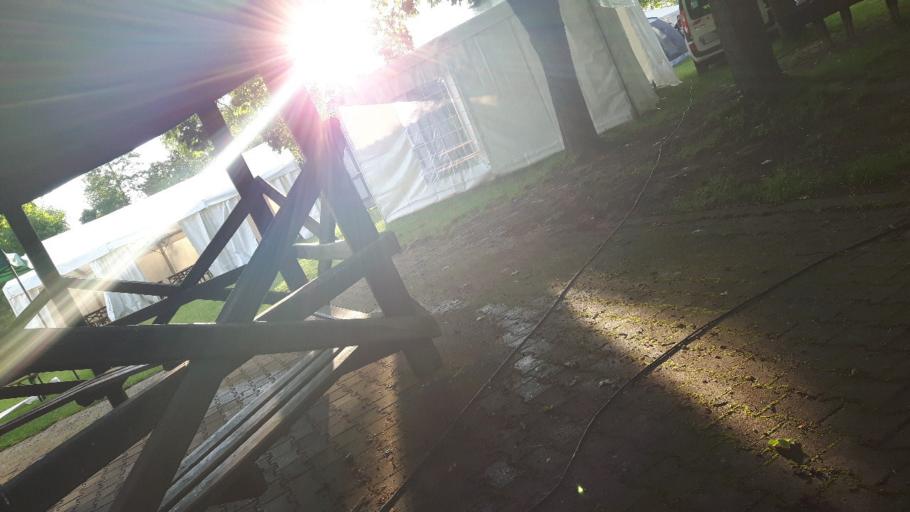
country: DE
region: Bavaria
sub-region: Regierungsbezirk Unterfranken
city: Sulzfeld
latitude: 50.2530
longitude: 10.4102
